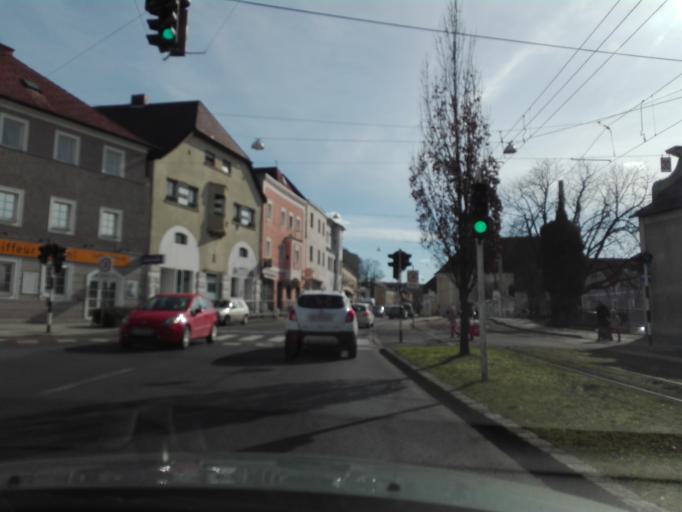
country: AT
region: Upper Austria
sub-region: Politischer Bezirk Linz-Land
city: Ansfelden
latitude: 48.2468
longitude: 14.3263
